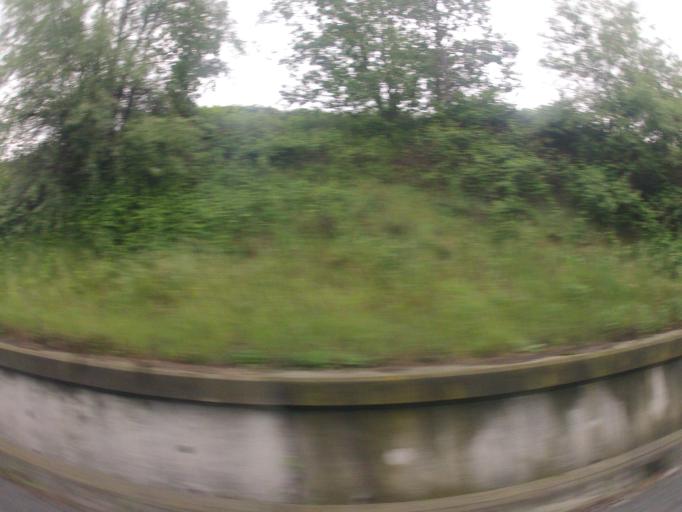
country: IT
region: Piedmont
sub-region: Provincia di Torino
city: La Loggia
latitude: 44.9480
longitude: 7.6792
